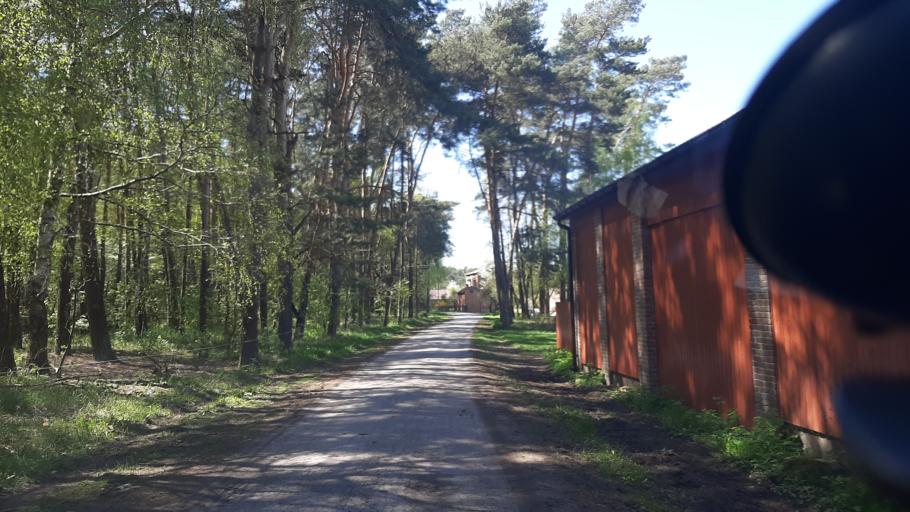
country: PL
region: Lublin Voivodeship
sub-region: Powiat lubartowski
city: Abramow
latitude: 51.4259
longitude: 22.2833
